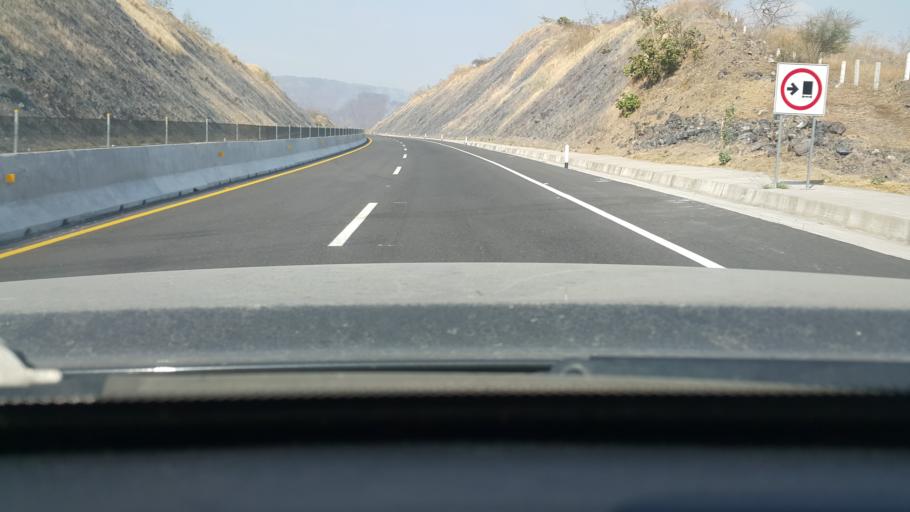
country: MX
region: Nayarit
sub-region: Ahuacatlan
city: Ahuacatlan
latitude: 21.0686
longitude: -104.4611
